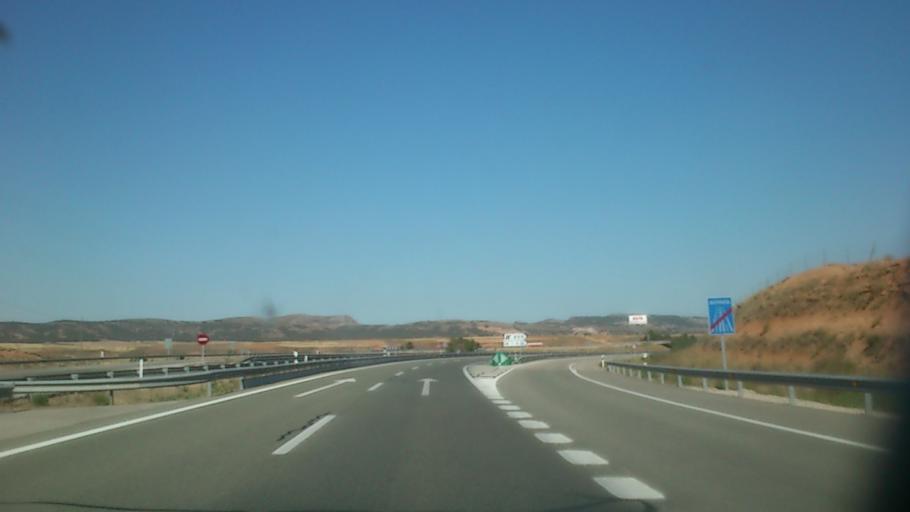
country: ES
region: Aragon
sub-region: Provincia de Zaragoza
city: Cetina
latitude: 41.3049
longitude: -1.9706
